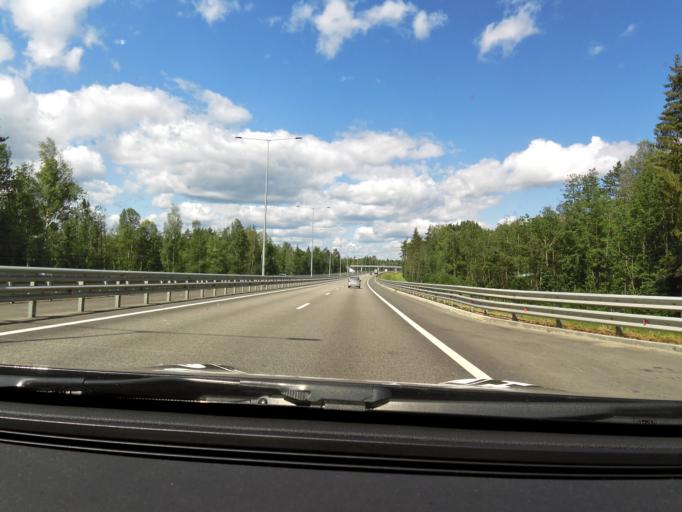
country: RU
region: Tverskaya
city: Vyshniy Volochek
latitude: 57.3802
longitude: 34.5714
